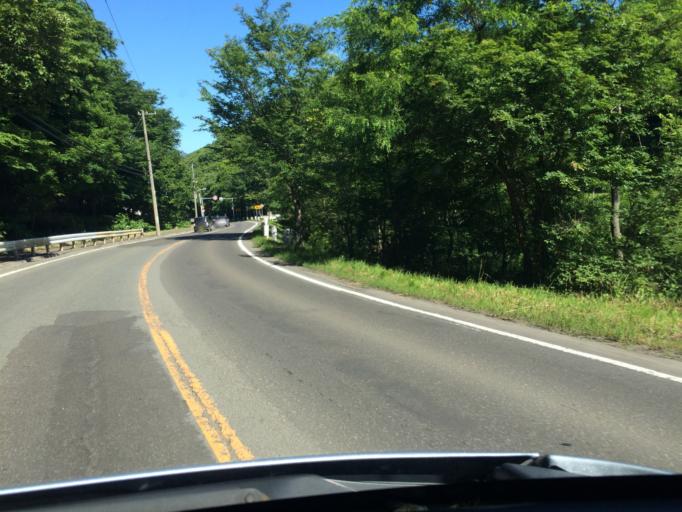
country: JP
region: Hokkaido
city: Sapporo
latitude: 43.0297
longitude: 141.2839
